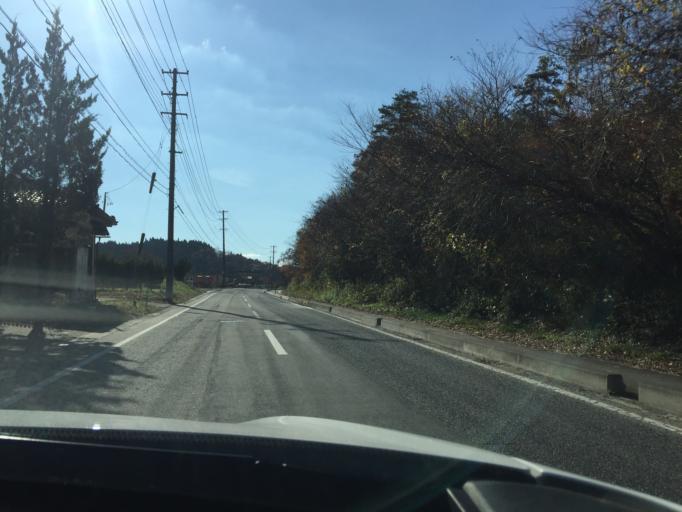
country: JP
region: Fukushima
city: Ishikawa
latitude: 37.2276
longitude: 140.5676
